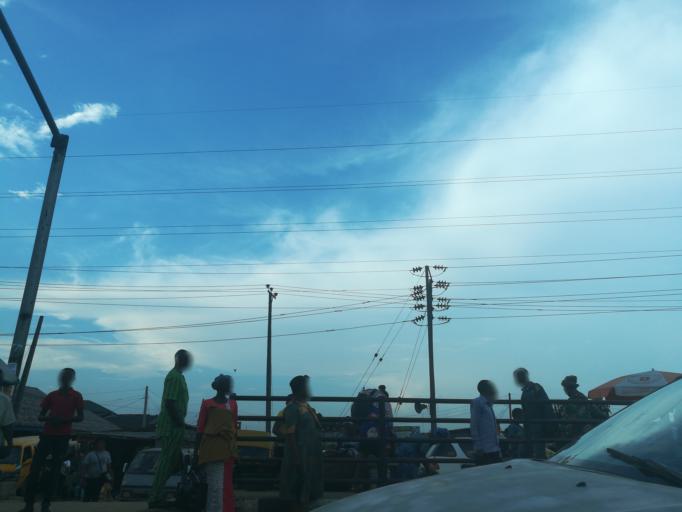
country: NG
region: Lagos
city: Ikorodu
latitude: 6.6258
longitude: 3.4851
